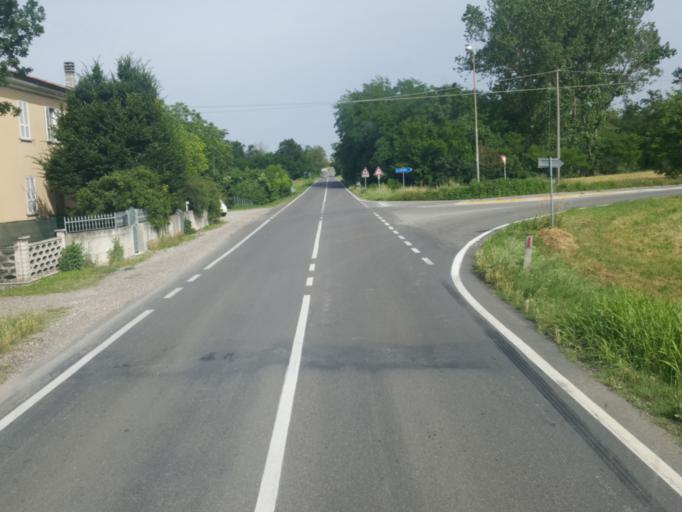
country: IT
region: Emilia-Romagna
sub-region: Provincia di Piacenza
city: Niviano
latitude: 44.9392
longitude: 9.6413
